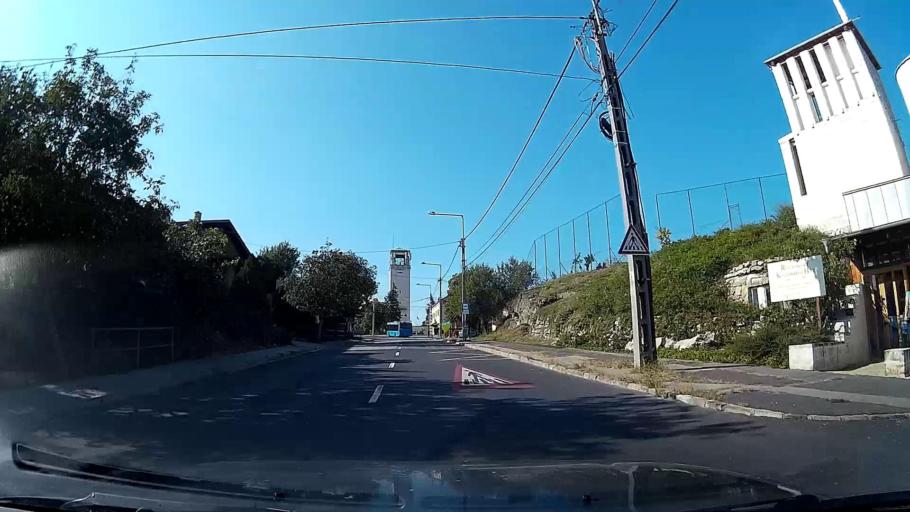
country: HU
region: Budapest
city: Budapest XXII. keruelet
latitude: 47.4129
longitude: 19.0182
